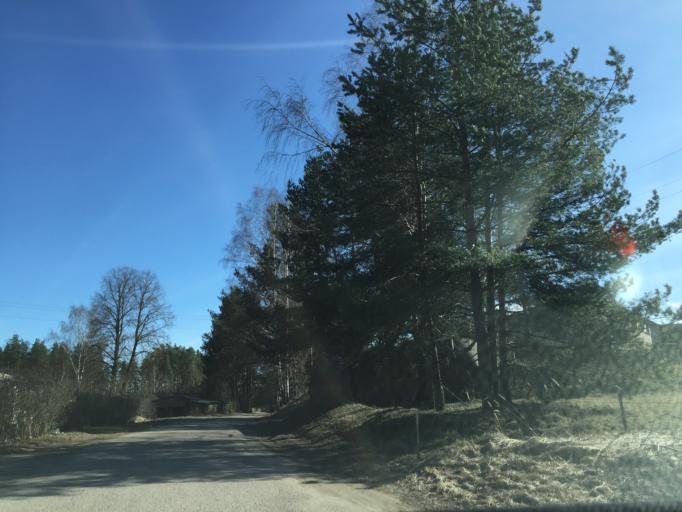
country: LV
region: Ikskile
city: Ikskile
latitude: 56.8440
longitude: 24.5030
